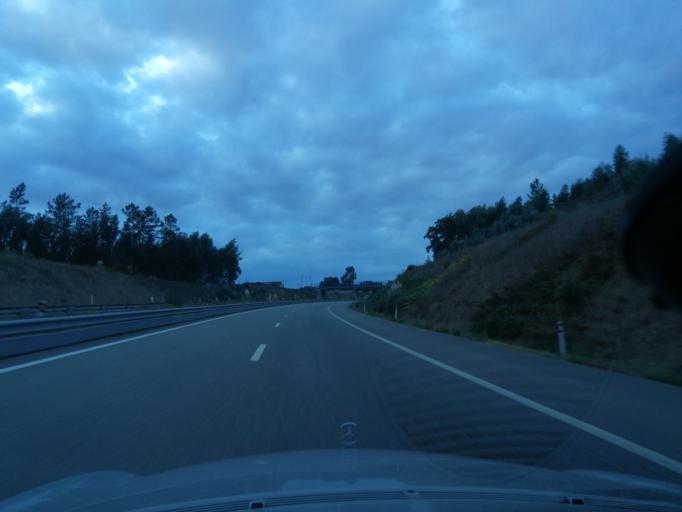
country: PT
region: Aveiro
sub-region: Estarreja
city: Beduido
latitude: 40.7646
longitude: -8.5512
